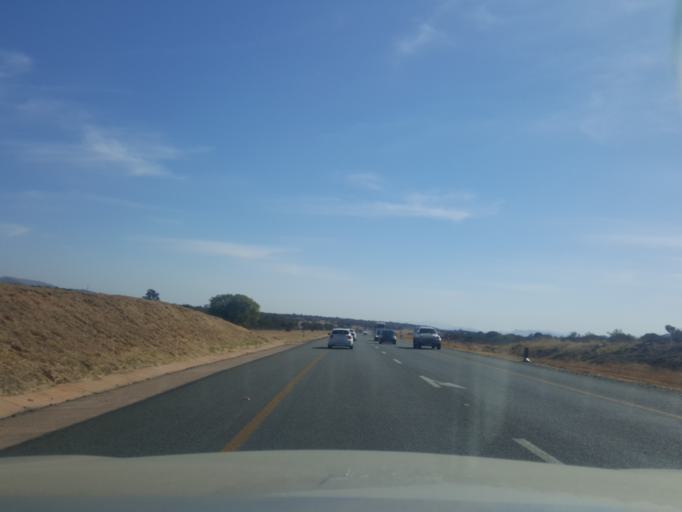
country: ZA
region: North-West
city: Ga-Rankuwa
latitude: -25.6592
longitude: 28.0117
